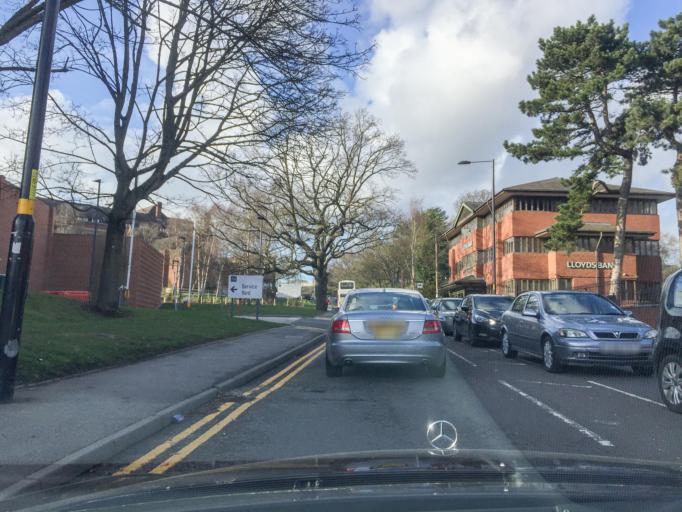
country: GB
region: England
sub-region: City and Borough of Birmingham
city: Birmingham
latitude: 52.4481
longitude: -1.9257
